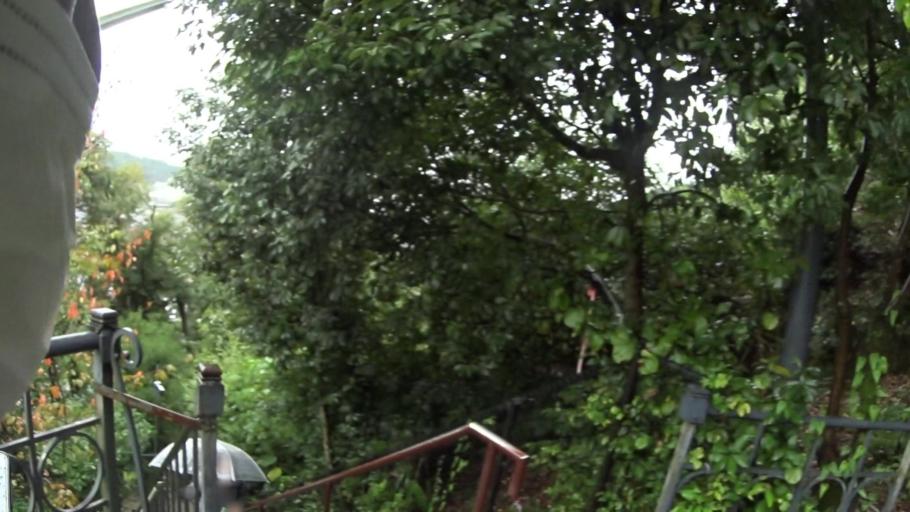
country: JP
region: Shiga Prefecture
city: Otsu-shi
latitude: 34.9852
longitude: 135.8085
